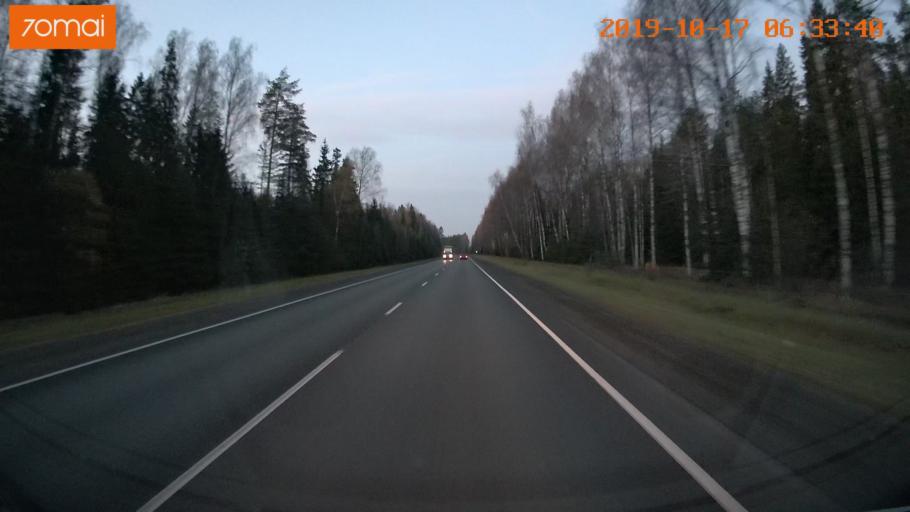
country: RU
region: Ivanovo
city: Novoye Leushino
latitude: 56.7108
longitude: 40.6535
